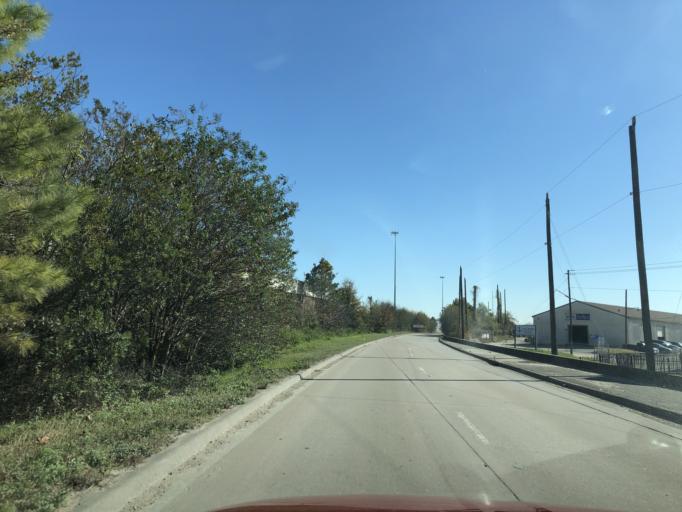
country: US
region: Texas
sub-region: Harris County
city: Cloverleaf
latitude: 29.7683
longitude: -95.1516
